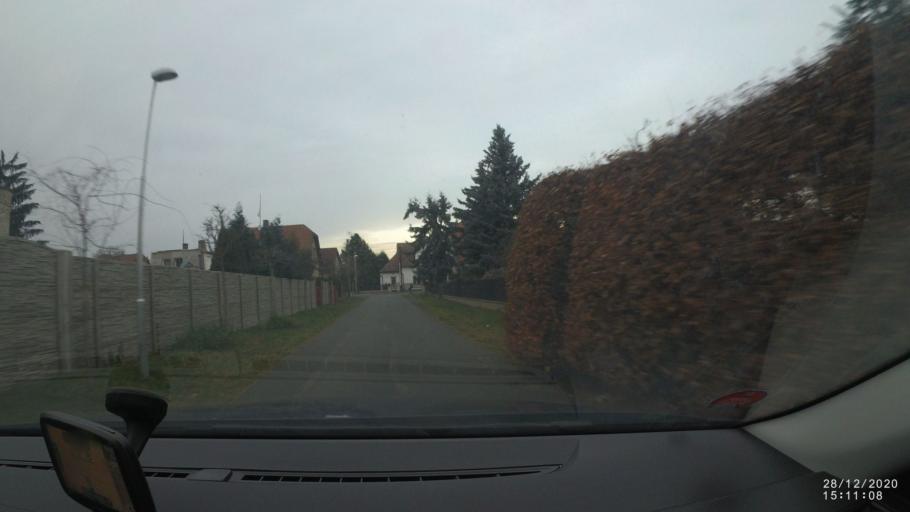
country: CZ
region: Central Bohemia
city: Uvaly
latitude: 50.0666
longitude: 14.7313
